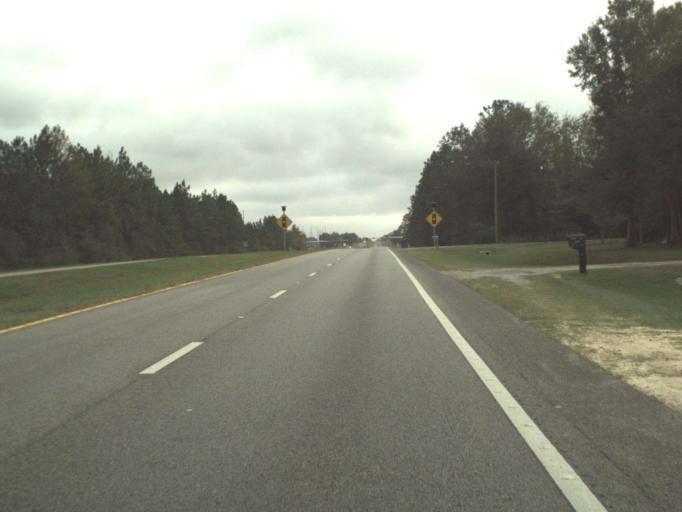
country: US
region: Florida
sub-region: Escambia County
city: Molino
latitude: 30.7359
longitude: -87.3492
